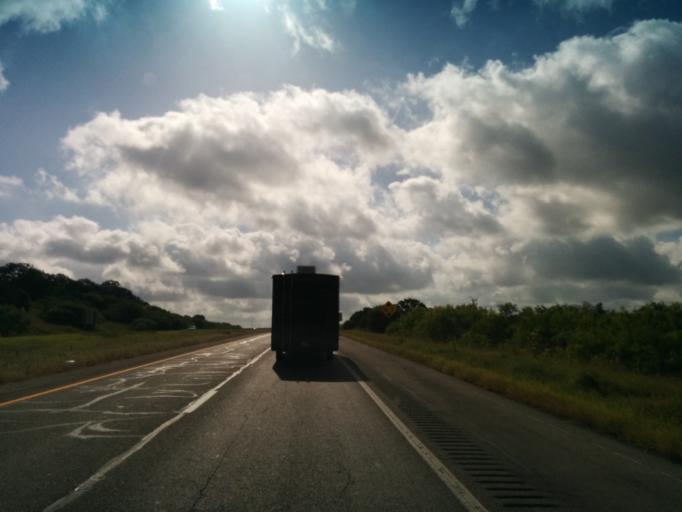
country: US
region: Texas
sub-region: Guadalupe County
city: Seguin
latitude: 29.6148
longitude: -97.8169
